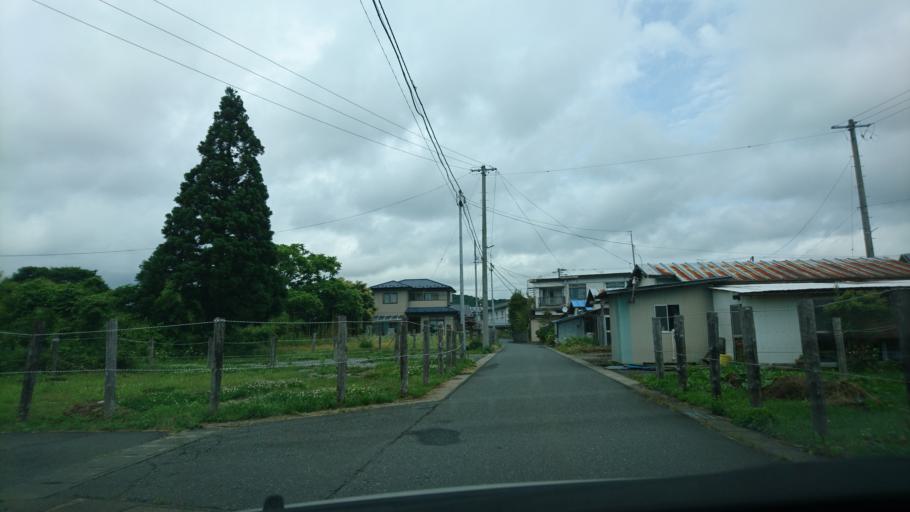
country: JP
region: Iwate
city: Ichinoseki
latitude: 38.9315
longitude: 141.1098
